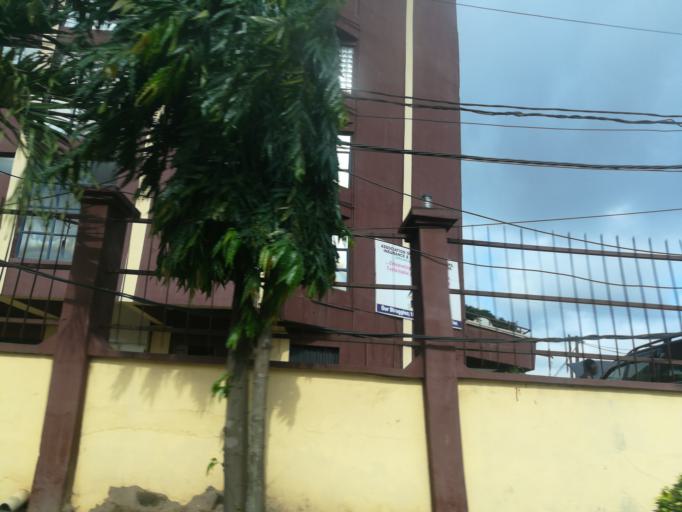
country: NG
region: Lagos
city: Ikeja
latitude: 6.6184
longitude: 3.3559
